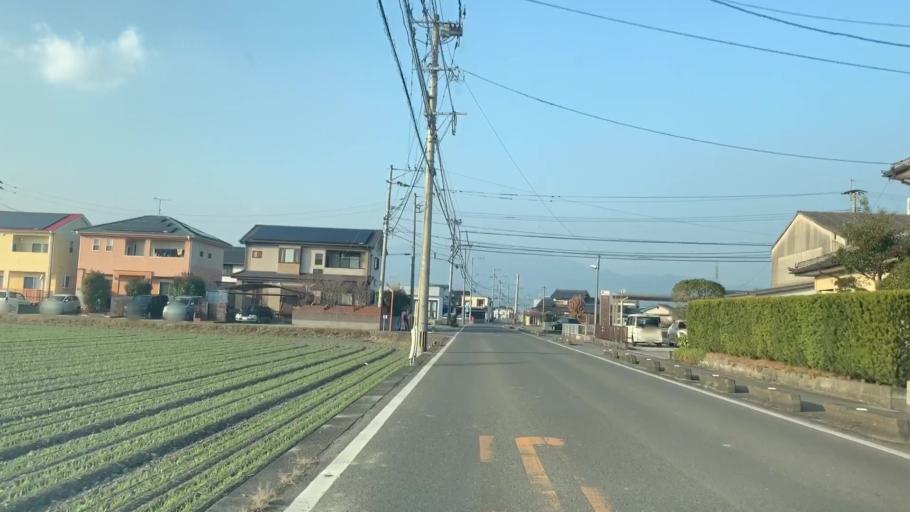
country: JP
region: Saga Prefecture
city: Saga-shi
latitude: 33.2643
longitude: 130.2311
